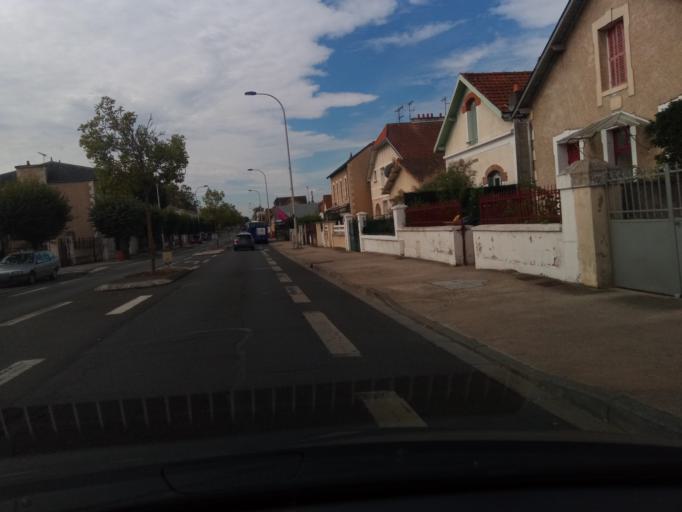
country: FR
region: Poitou-Charentes
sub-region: Departement de la Vienne
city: Biard
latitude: 46.5618
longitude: 0.3152
